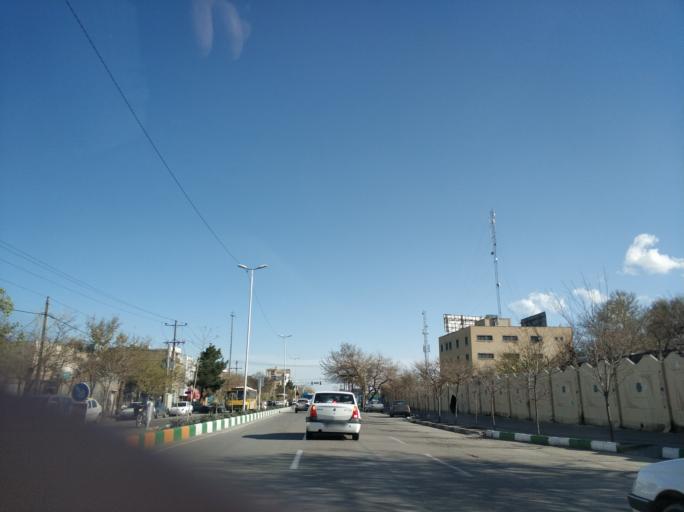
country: IR
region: Razavi Khorasan
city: Mashhad
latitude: 36.3002
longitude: 59.6326
